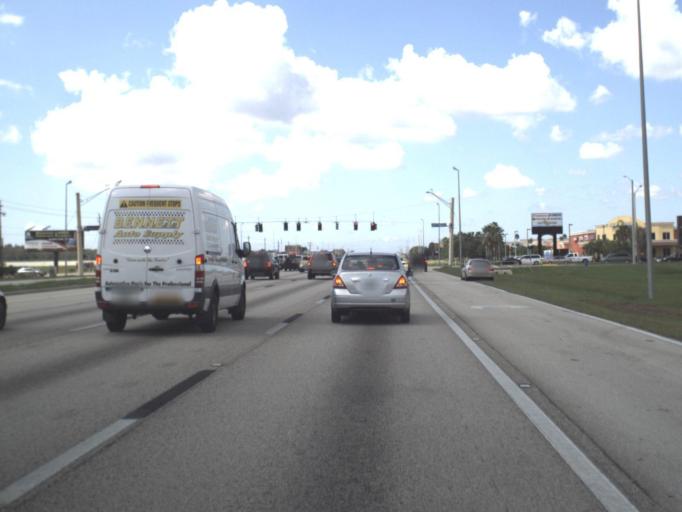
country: US
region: Florida
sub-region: Lee County
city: Fort Myers
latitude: 26.5977
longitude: -81.8395
